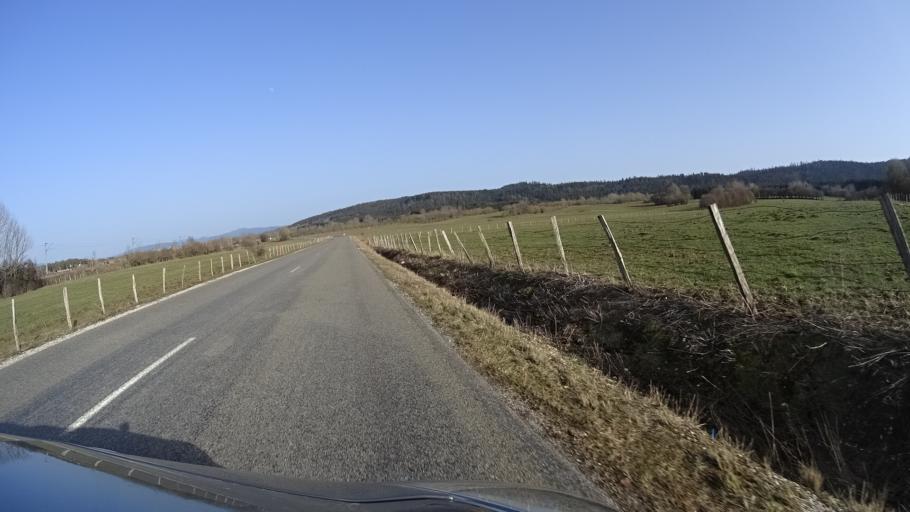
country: FR
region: Franche-Comte
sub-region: Departement du Doubs
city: Frasne
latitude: 46.8670
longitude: 6.2360
